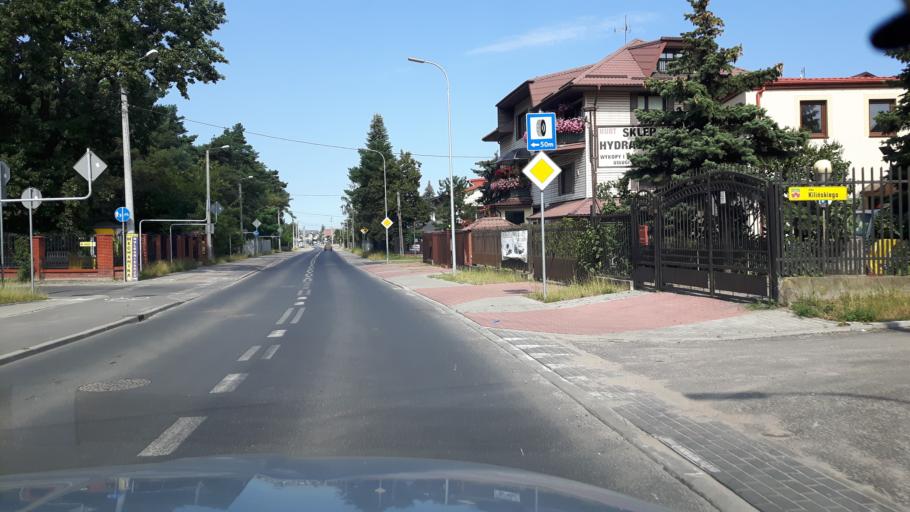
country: PL
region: Masovian Voivodeship
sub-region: Powiat wolominski
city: Marki
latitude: 52.3189
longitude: 21.0984
